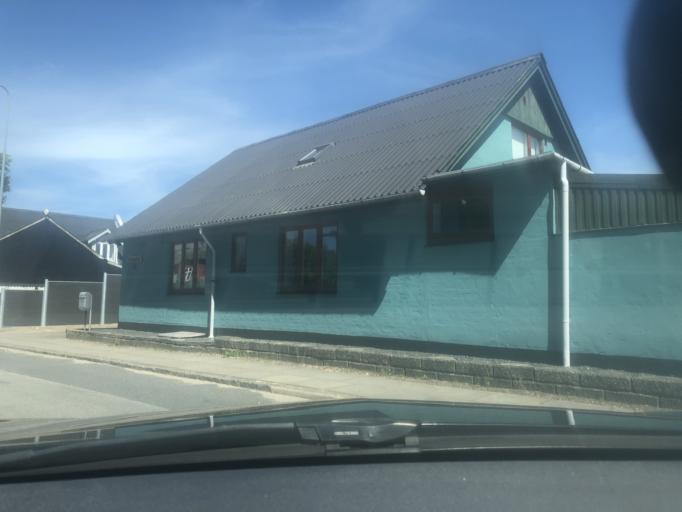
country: DK
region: South Denmark
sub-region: Vejle Kommune
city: Jelling
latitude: 55.7008
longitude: 9.3822
